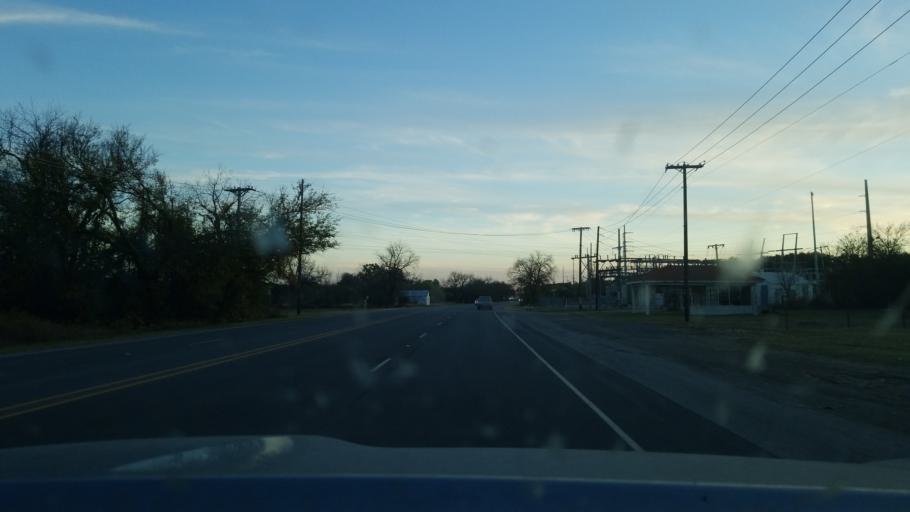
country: US
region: Texas
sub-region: Stephens County
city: Breckenridge
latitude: 32.7489
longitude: -98.9026
